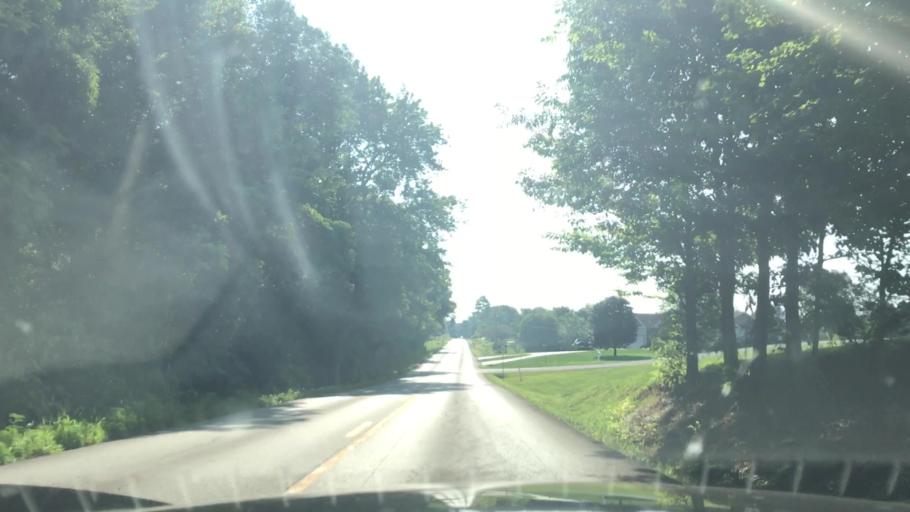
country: US
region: Kentucky
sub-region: Hart County
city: Horse Cave
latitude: 37.1673
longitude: -85.8147
